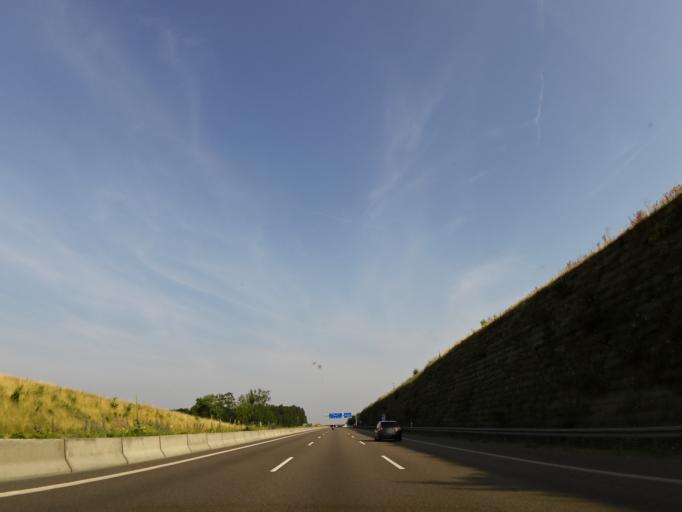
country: DE
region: Baden-Wuerttemberg
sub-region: Regierungsbezirk Stuttgart
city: Rutesheim
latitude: 48.8072
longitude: 8.9289
